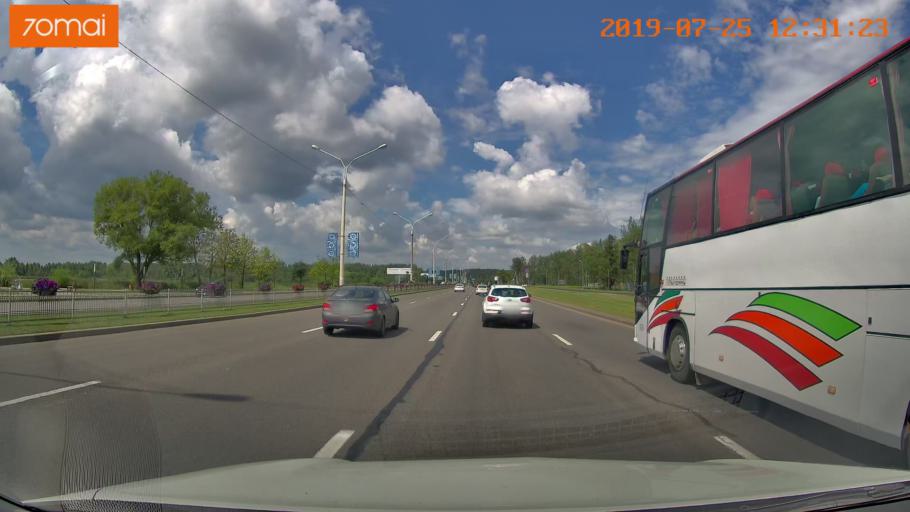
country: BY
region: Minsk
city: Zhdanovichy
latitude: 53.9460
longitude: 27.4576
